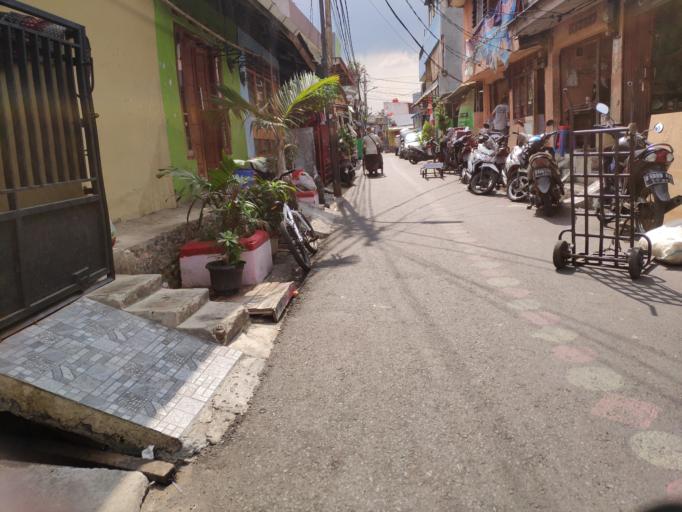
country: ID
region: Jakarta Raya
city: Jakarta
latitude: -6.1959
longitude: 106.8610
